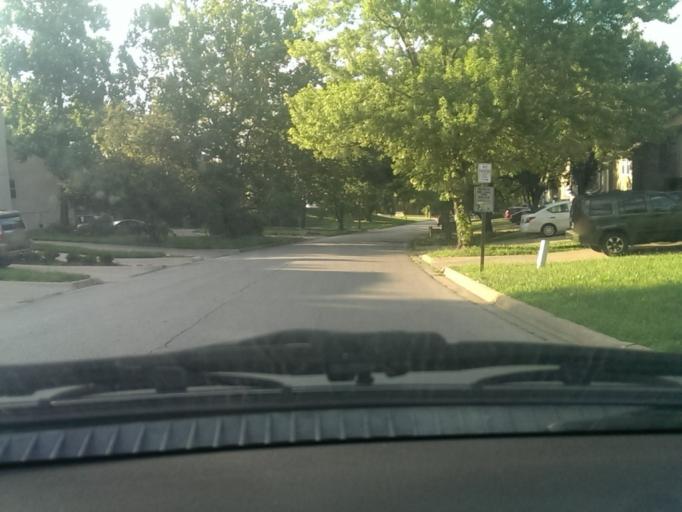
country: US
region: Kansas
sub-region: Johnson County
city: Westwood
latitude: 39.0677
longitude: -94.6097
